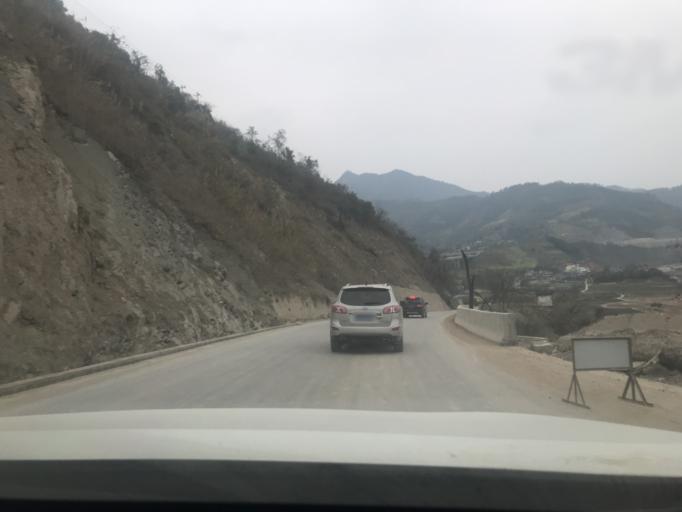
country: CN
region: Guangxi Zhuangzu Zizhiqu
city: Xinzhou
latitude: 25.0186
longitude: 105.8627
